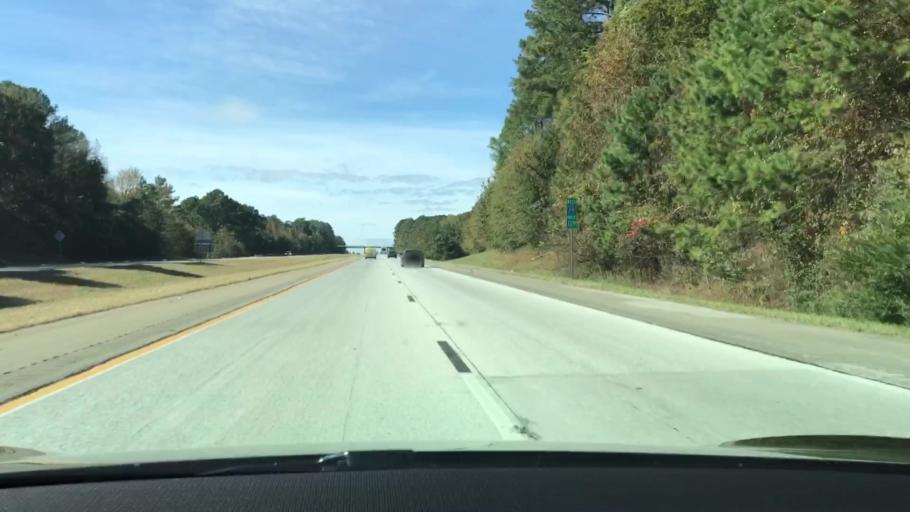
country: US
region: Georgia
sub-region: Greene County
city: Greensboro
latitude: 33.5412
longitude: -83.2274
